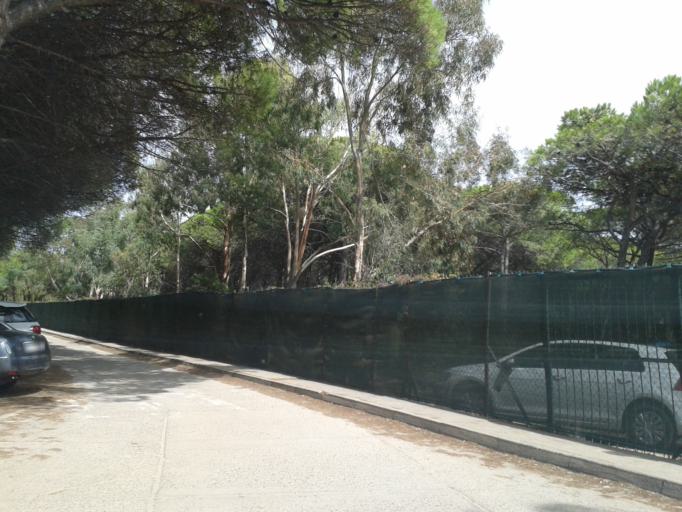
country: IT
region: Sardinia
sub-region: Provincia di Cagliari
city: Villasimius
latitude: 39.1222
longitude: 9.5112
